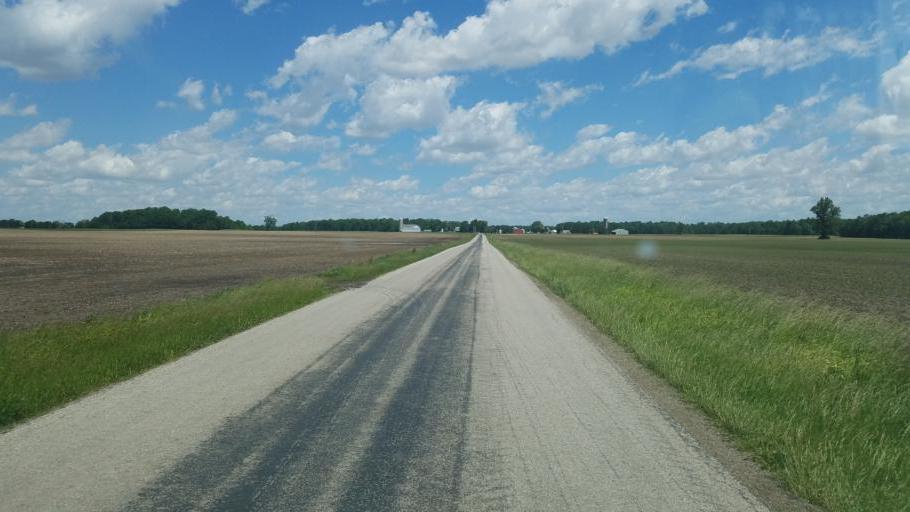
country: US
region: Ohio
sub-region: Richland County
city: Shelby
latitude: 40.9223
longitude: -82.7049
